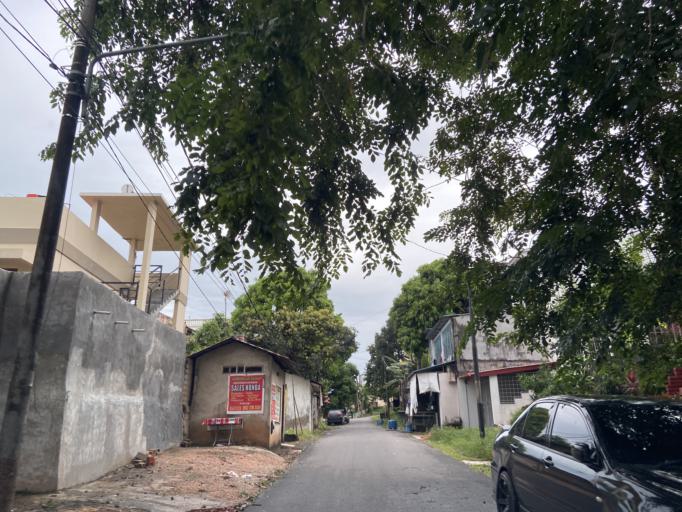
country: SG
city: Singapore
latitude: 1.1310
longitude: 104.0130
